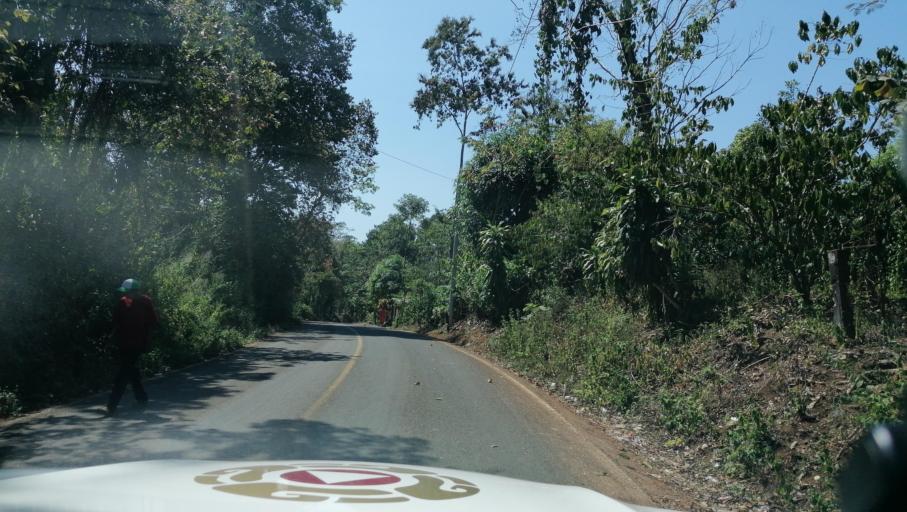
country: MX
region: Chiapas
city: Veinte de Noviembre
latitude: 15.0095
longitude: -92.2290
